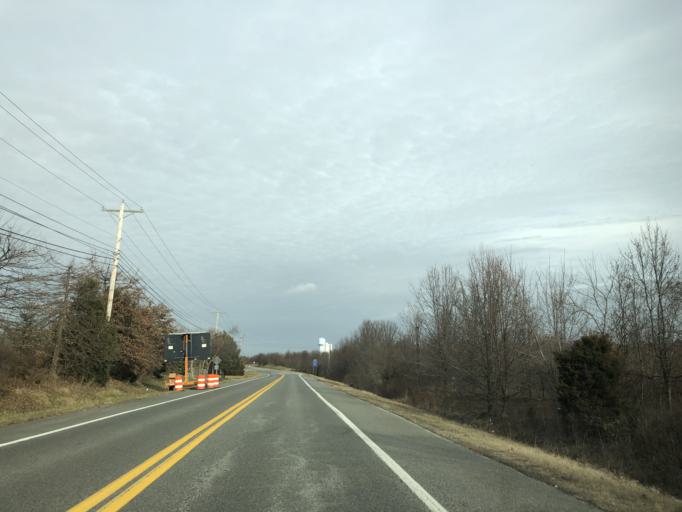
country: US
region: Delaware
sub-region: New Castle County
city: Middletown
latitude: 39.5099
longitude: -75.6505
